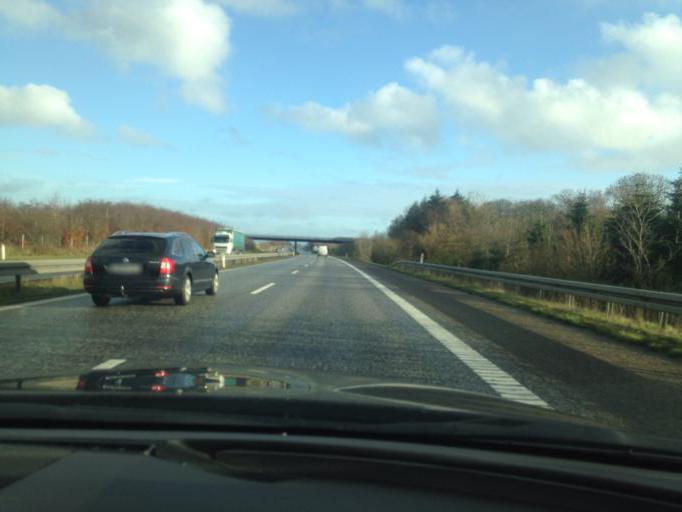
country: DK
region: South Denmark
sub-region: Kolding Kommune
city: Lunderskov
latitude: 55.4984
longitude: 9.2318
